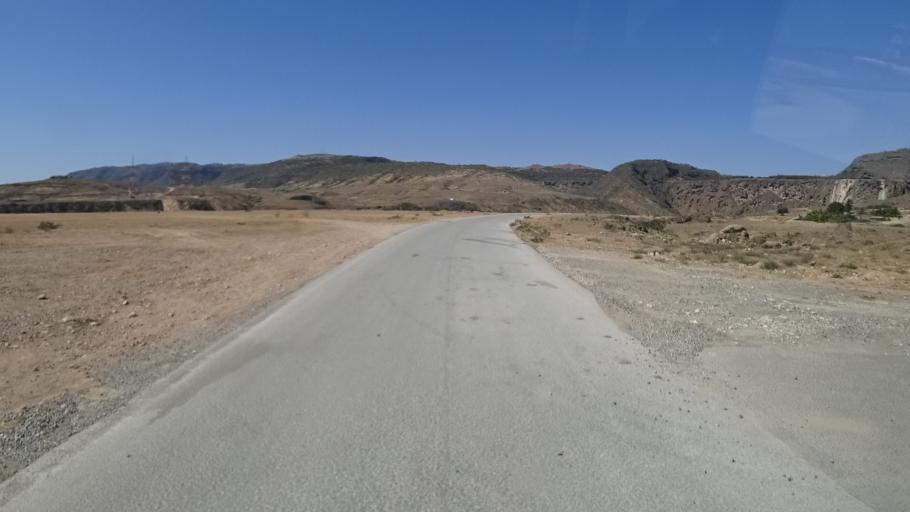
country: OM
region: Zufar
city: Salalah
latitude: 17.0619
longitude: 54.4310
